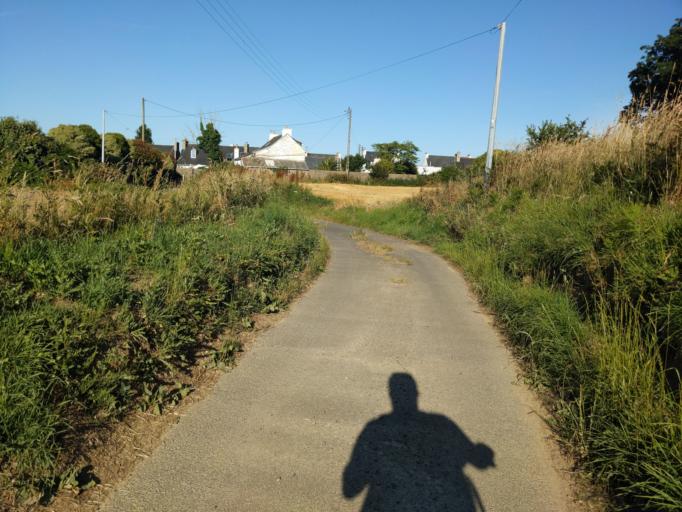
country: FR
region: Brittany
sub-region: Departement des Cotes-d'Armor
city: Pleubian
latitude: 48.8454
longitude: -3.1400
